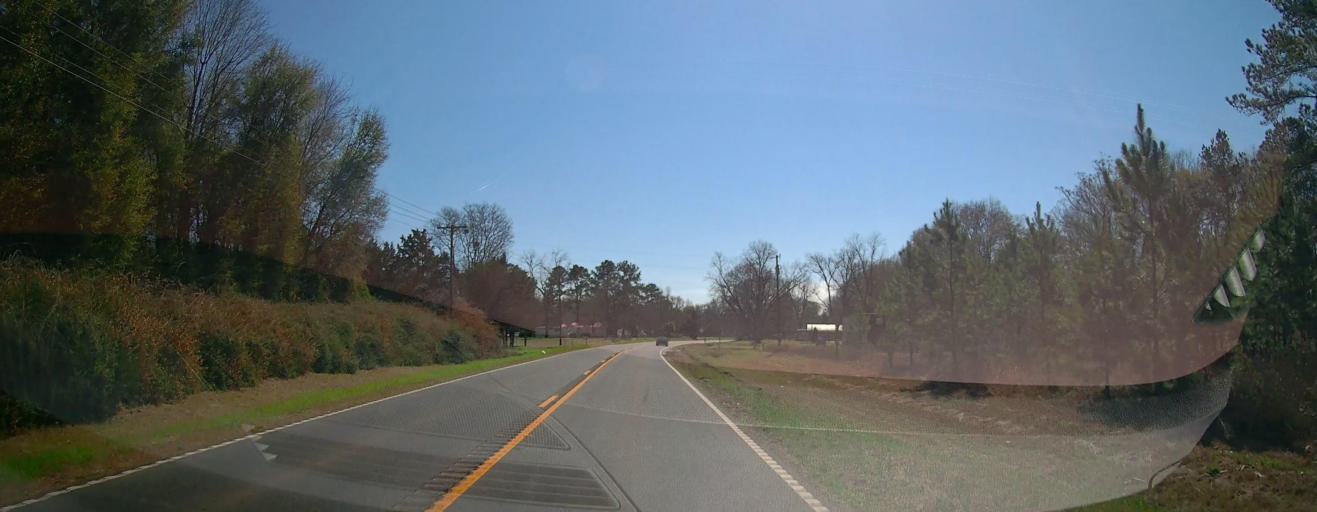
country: US
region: Georgia
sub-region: Houston County
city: Perry
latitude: 32.4587
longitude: -83.6184
